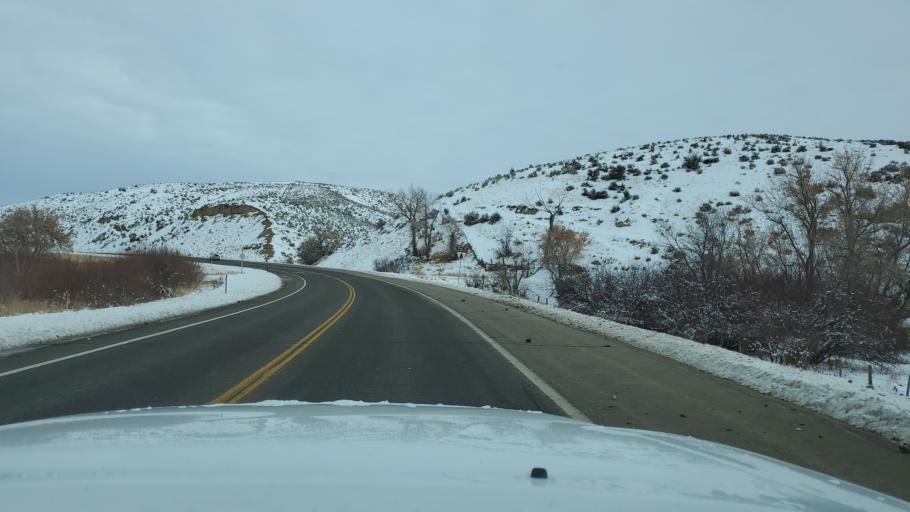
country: US
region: Colorado
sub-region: Routt County
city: Hayden
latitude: 40.5041
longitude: -107.3780
